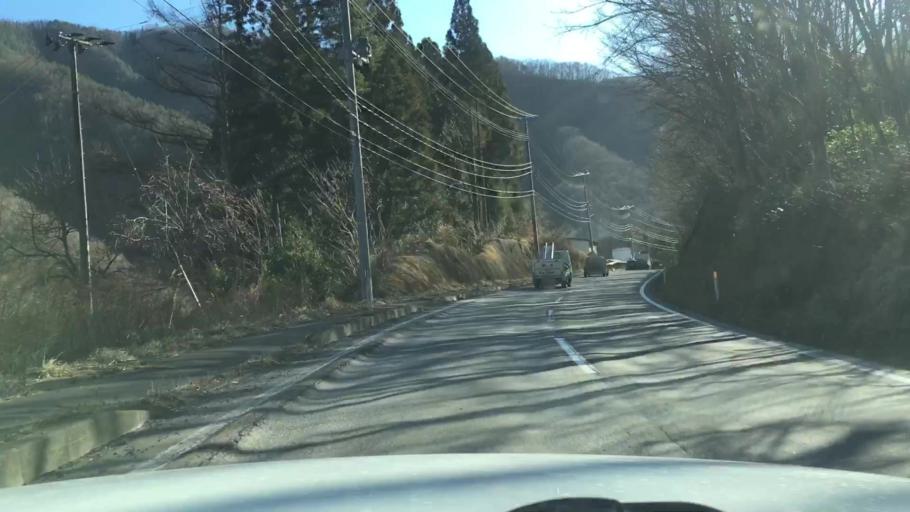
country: JP
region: Iwate
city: Miyako
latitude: 39.6224
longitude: 141.8109
